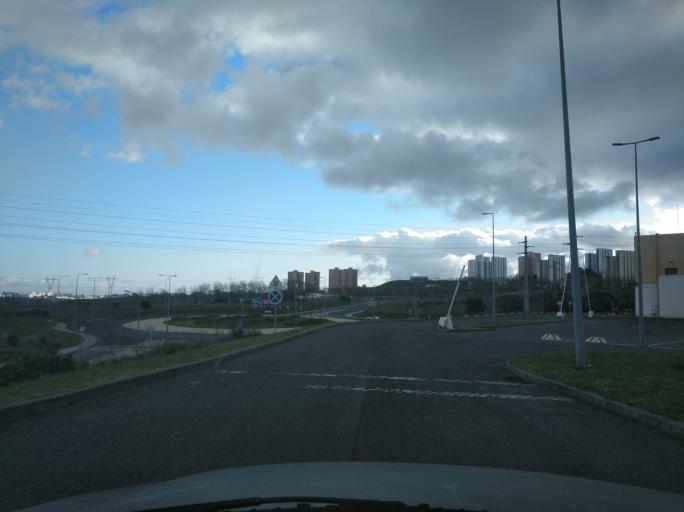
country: PT
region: Lisbon
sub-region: Loures
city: Loures
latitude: 38.8180
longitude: -9.1739
